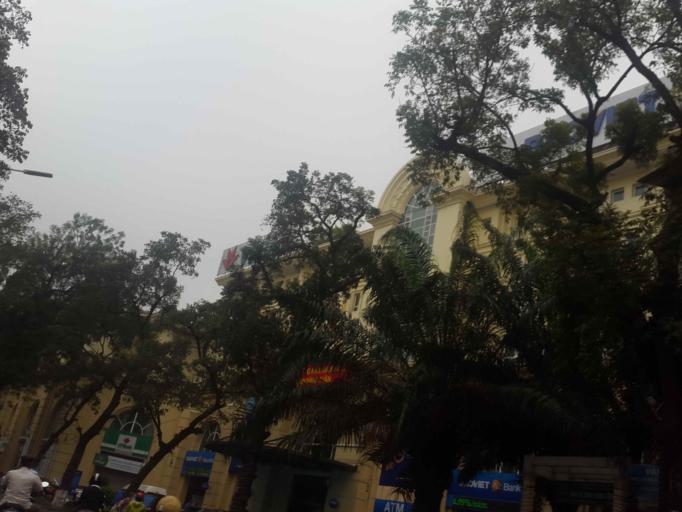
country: VN
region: Ha Noi
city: Hoan Kiem
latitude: 21.0314
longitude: 105.8509
